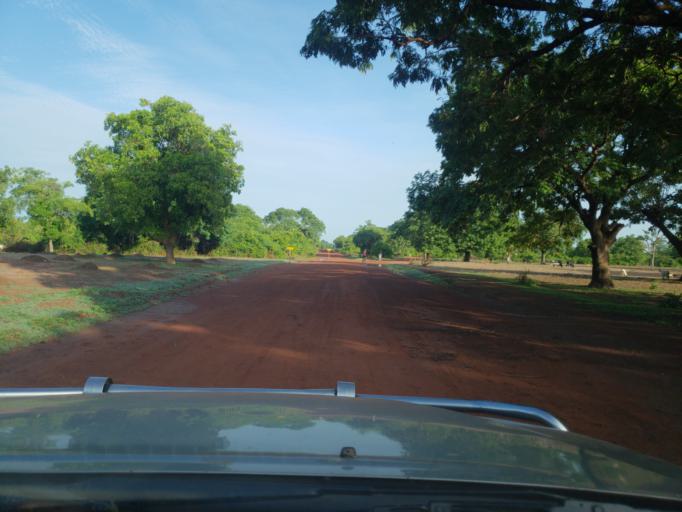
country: ML
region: Sikasso
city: Koutiala
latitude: 12.4218
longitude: -5.5856
